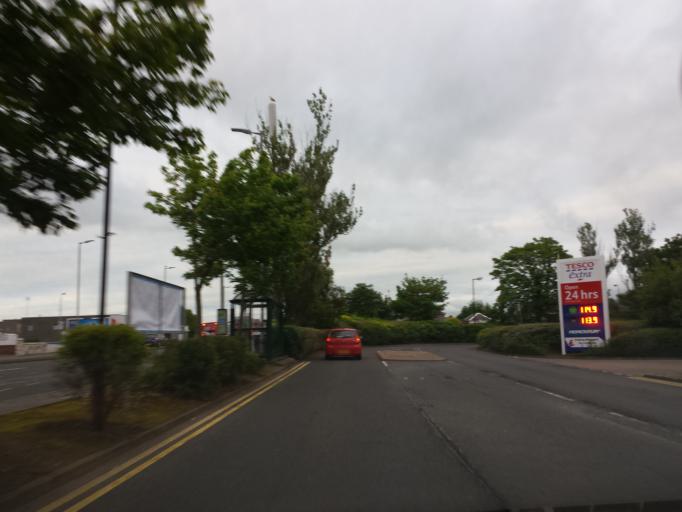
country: GB
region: Scotland
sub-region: South Ayrshire
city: Prestwick
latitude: 55.4689
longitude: -4.6088
